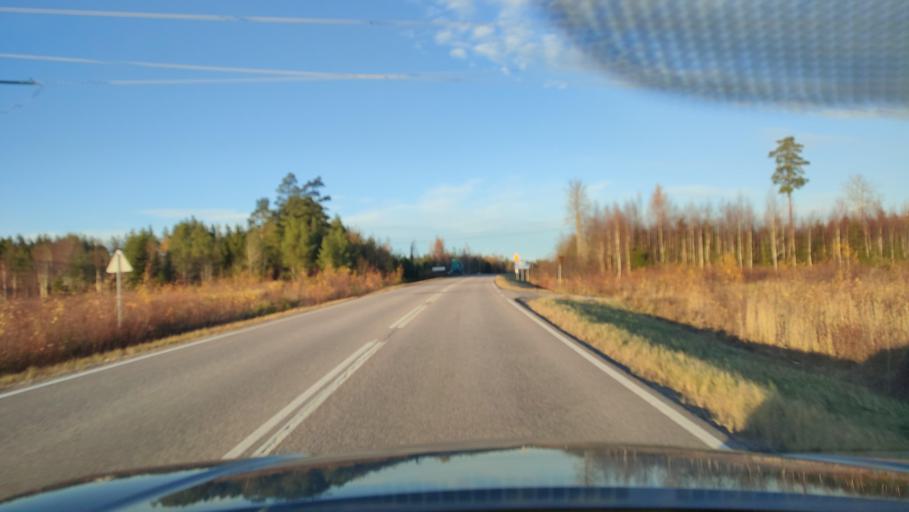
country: FI
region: Ostrobothnia
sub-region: Sydosterbotten
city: Kristinestad
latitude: 62.2922
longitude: 21.3799
